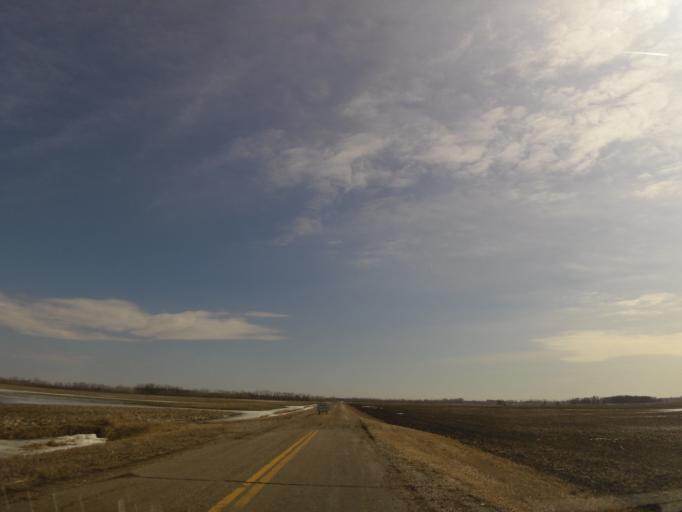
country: US
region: North Dakota
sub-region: Walsh County
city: Grafton
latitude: 48.3242
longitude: -97.1863
